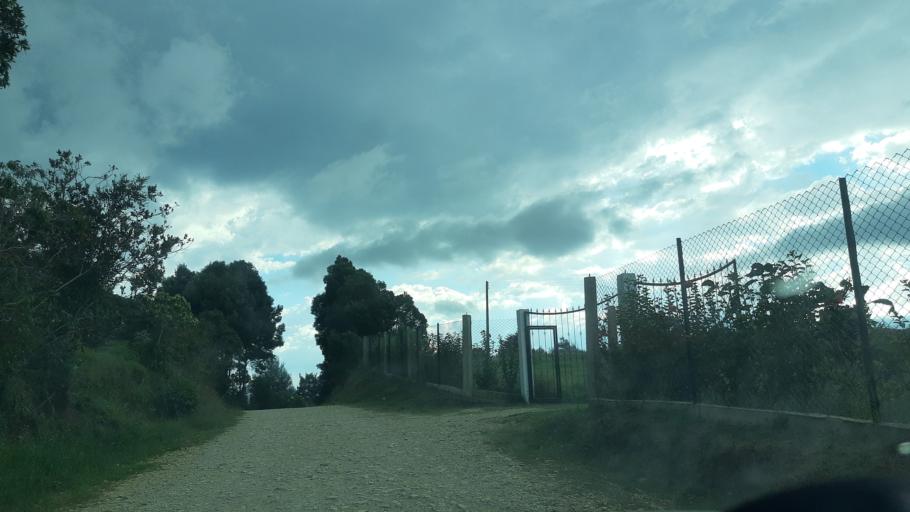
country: CO
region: Boyaca
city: Santa Sofia
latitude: 5.7478
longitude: -73.5591
